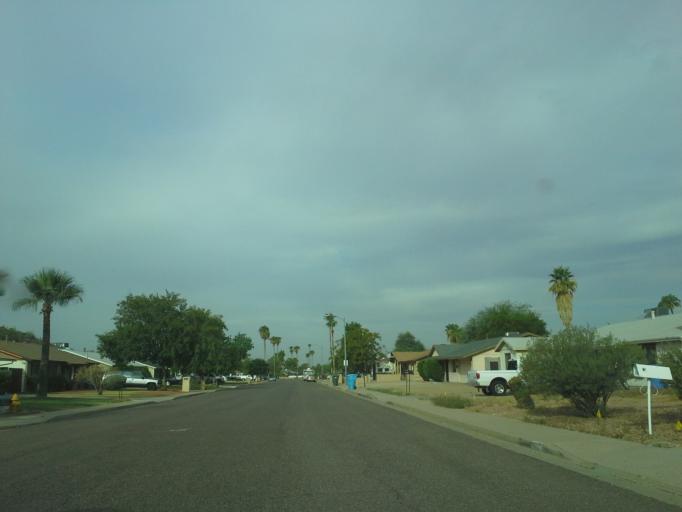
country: US
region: Arizona
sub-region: Maricopa County
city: Glendale
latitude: 33.6045
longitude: -112.0933
